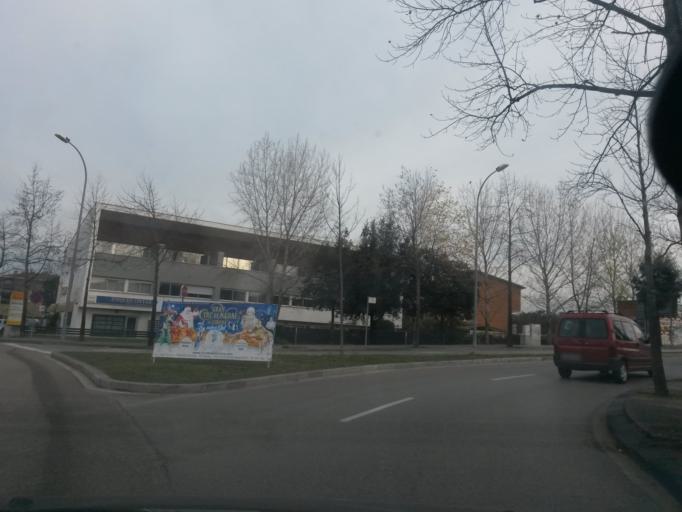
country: ES
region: Catalonia
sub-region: Provincia de Girona
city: Salt
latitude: 41.9607
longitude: 2.8110
